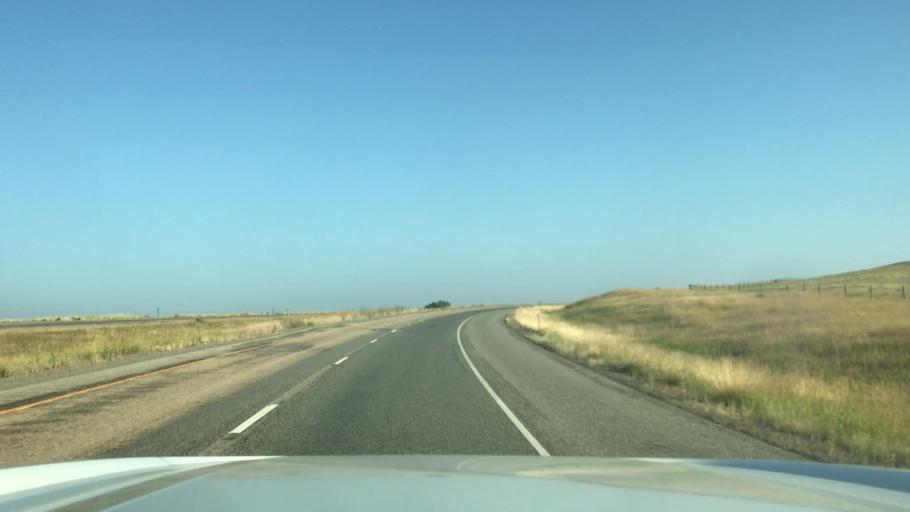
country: US
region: Montana
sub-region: Big Horn County
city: Crow Agency
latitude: 45.4850
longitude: -107.3783
